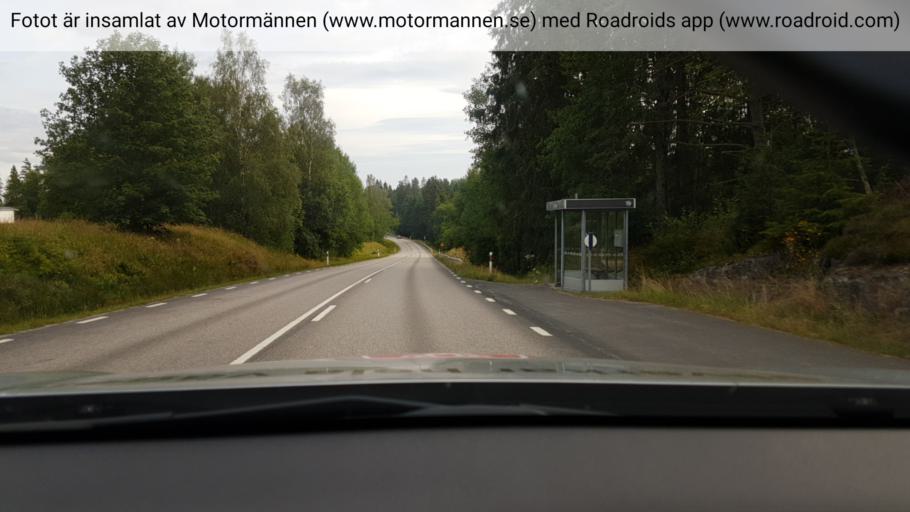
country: SE
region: Vaestra Goetaland
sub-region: Uddevalla Kommun
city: Uddevalla
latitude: 58.4319
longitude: 12.0186
